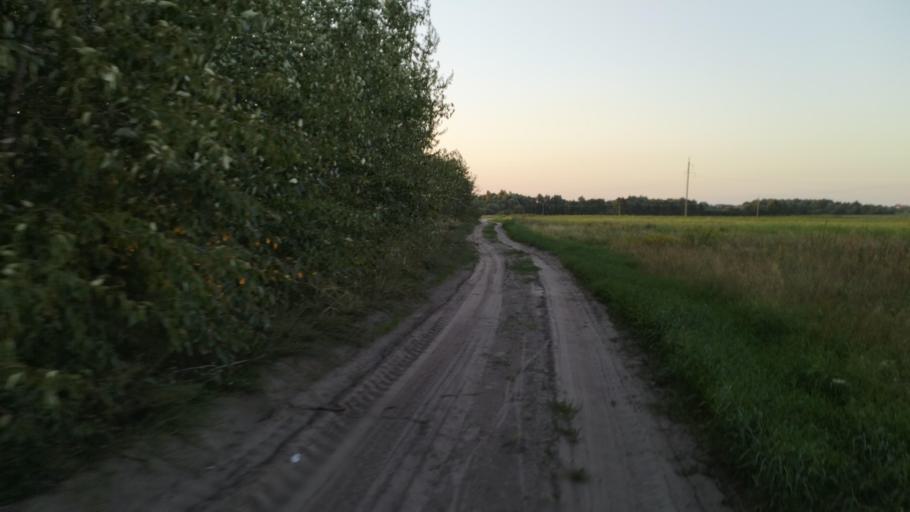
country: BY
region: Brest
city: Davyd-Haradok
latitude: 52.0329
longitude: 27.1934
